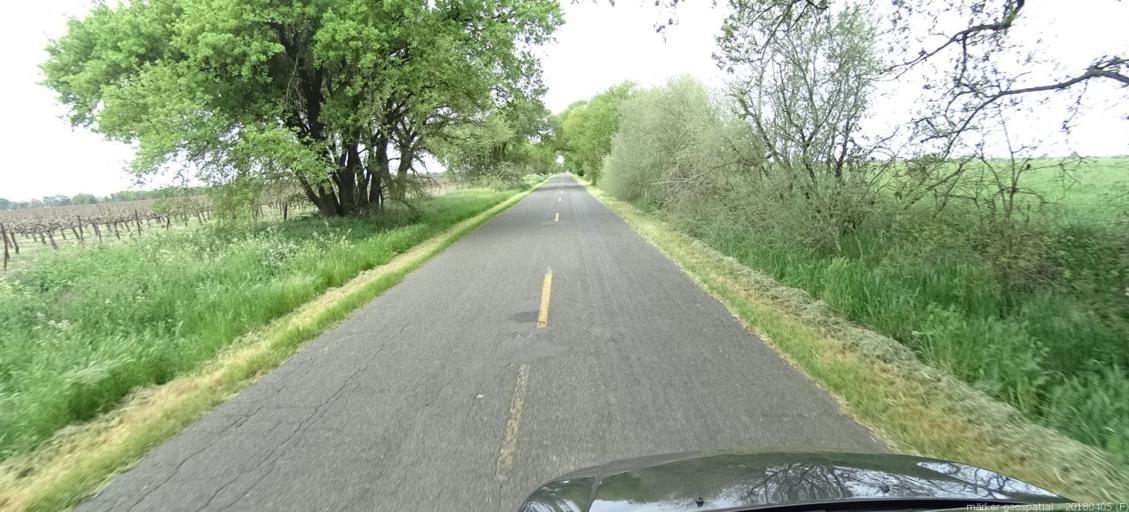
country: US
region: California
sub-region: Sacramento County
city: Galt
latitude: 38.2400
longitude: -121.3515
